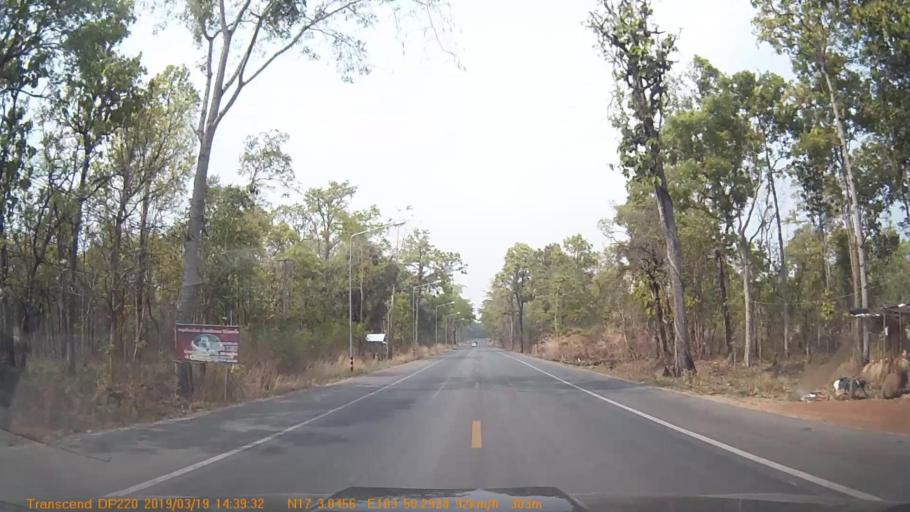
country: TH
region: Sakon Nakhon
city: Phu Phan
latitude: 17.0510
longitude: 103.9716
